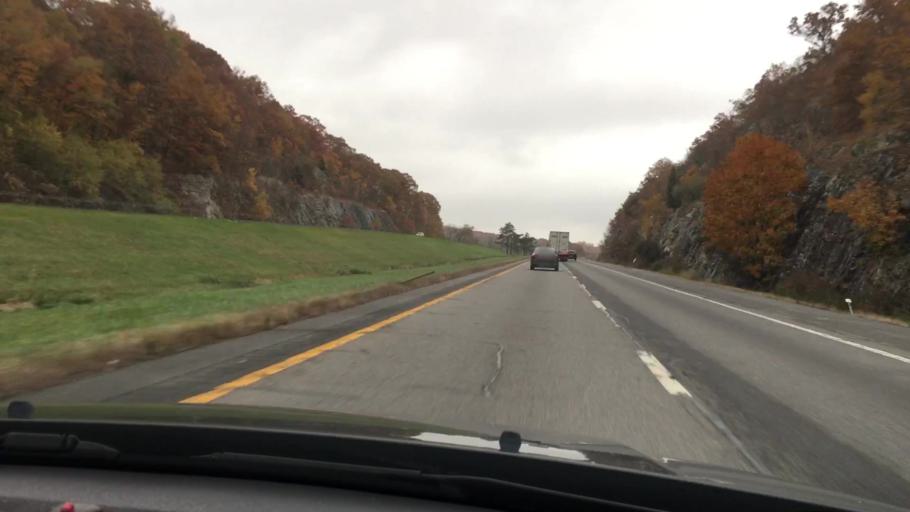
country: US
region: New York
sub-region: Putnam County
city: Lake Carmel
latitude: 41.4535
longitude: -73.6393
